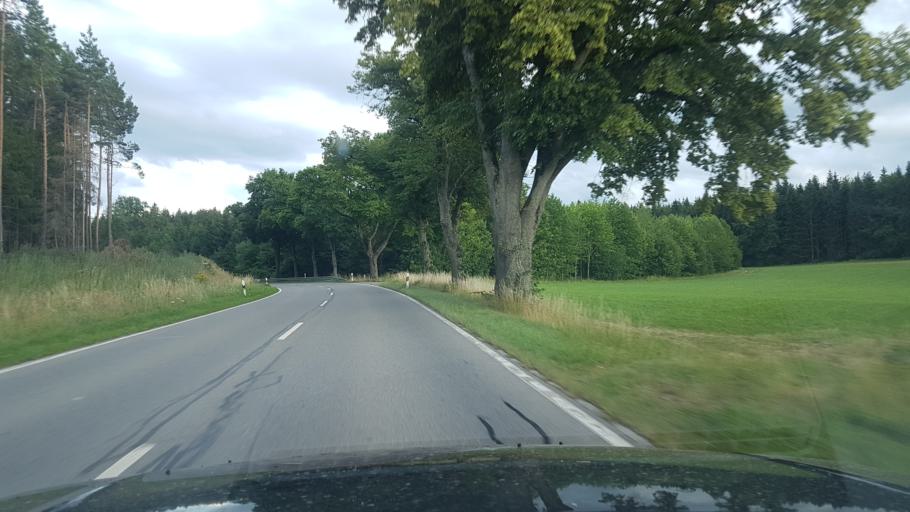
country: DE
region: Baden-Wuerttemberg
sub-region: Freiburg Region
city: Braunlingen
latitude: 47.9627
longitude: 8.4461
